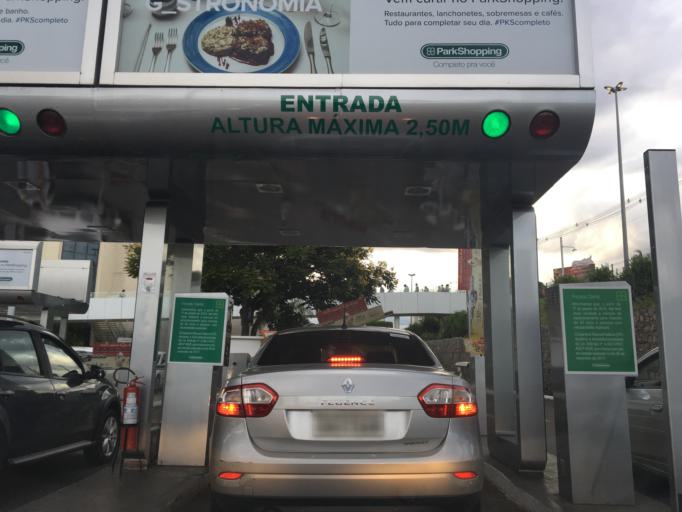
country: BR
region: Federal District
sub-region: Brasilia
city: Brasilia
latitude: -15.8324
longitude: -47.9540
